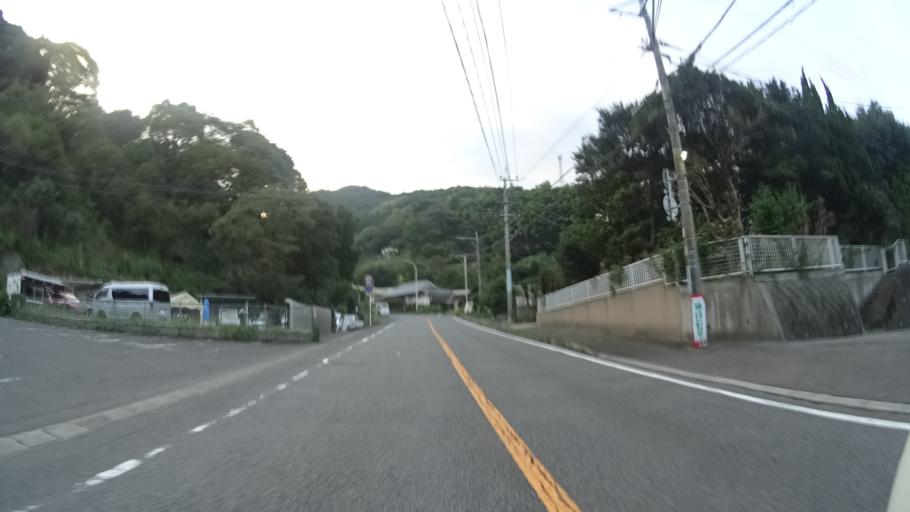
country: JP
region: Oita
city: Beppu
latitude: 33.3281
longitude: 131.4785
